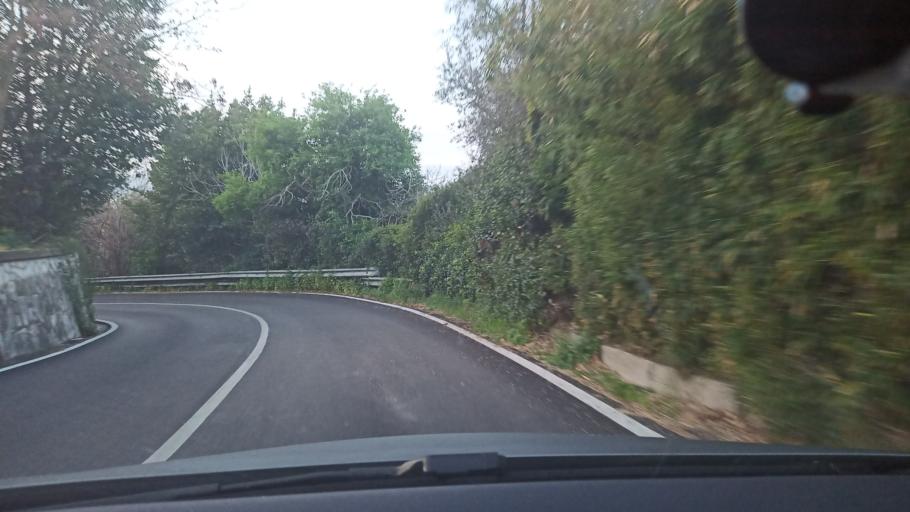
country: IT
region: Latium
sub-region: Provincia di Rieti
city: Torri in Sabina
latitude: 42.3331
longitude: 12.6450
